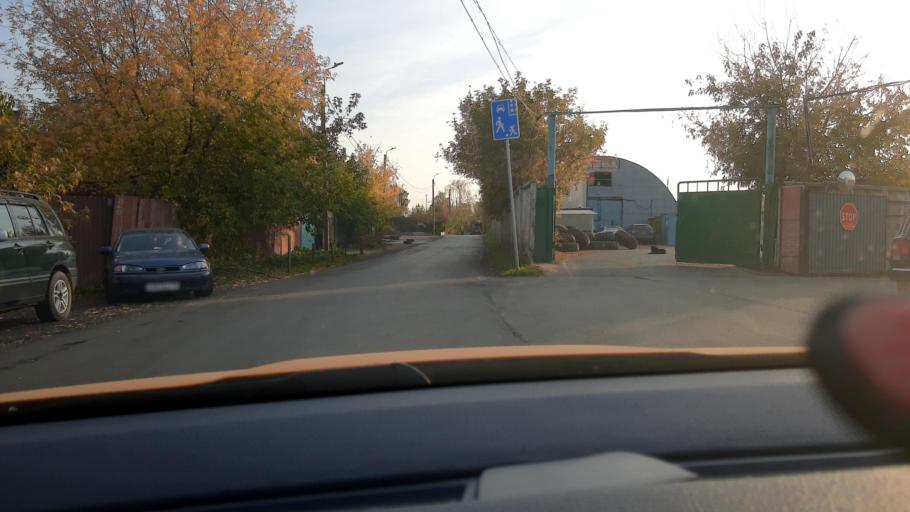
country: RU
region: Moscow
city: Strogino
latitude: 55.7875
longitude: 37.3980
